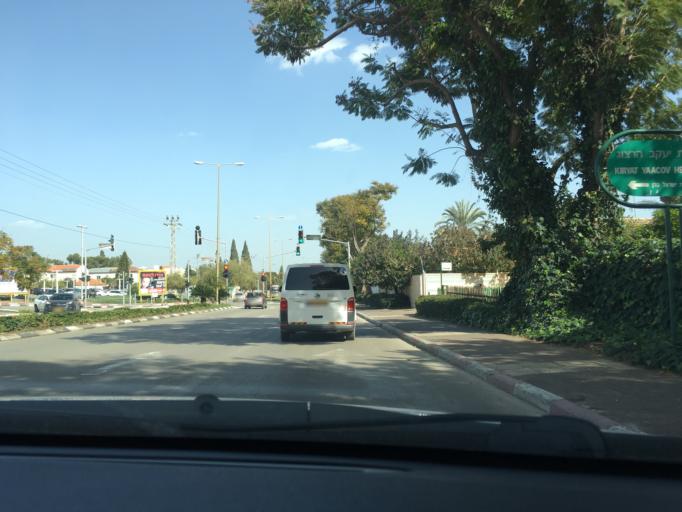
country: IL
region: Central District
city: Kfar Saba
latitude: 32.1815
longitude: 34.8982
